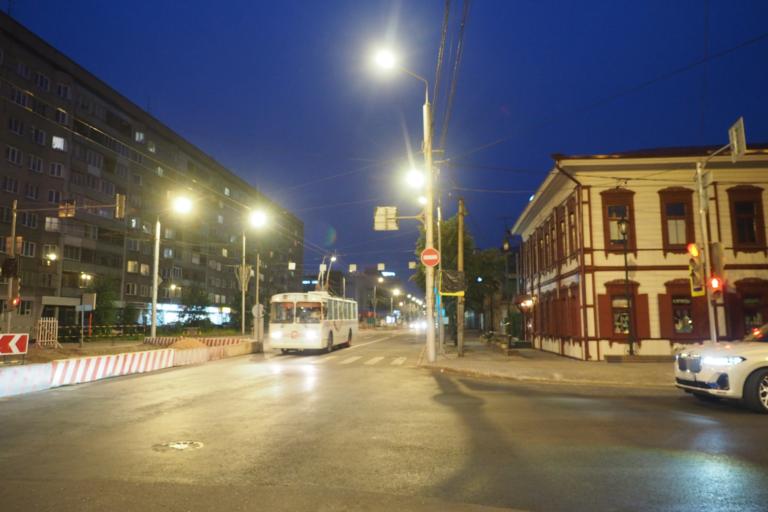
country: RU
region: Krasnoyarskiy
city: Krasnoyarsk
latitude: 56.0111
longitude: 92.8815
